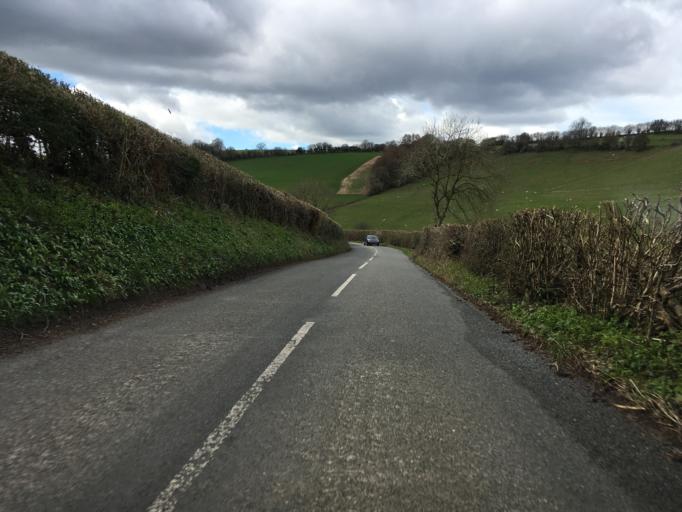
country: GB
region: England
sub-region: Gloucestershire
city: Coleford
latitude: 51.7528
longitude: -2.6410
